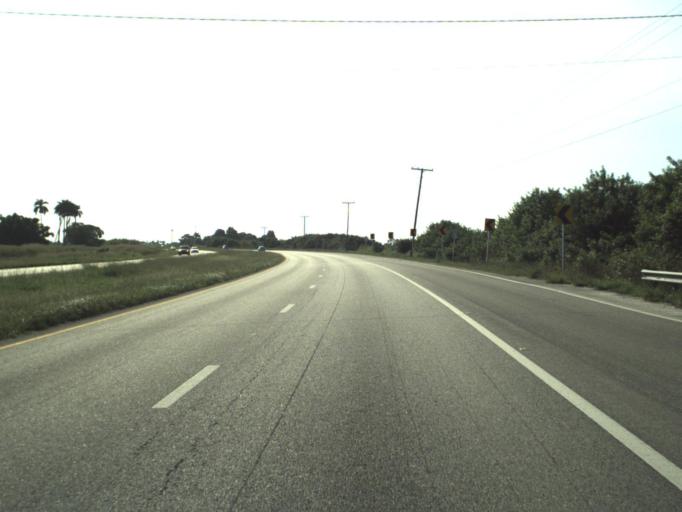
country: US
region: Florida
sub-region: Palm Beach County
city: South Bay
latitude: 26.6819
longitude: -80.7508
